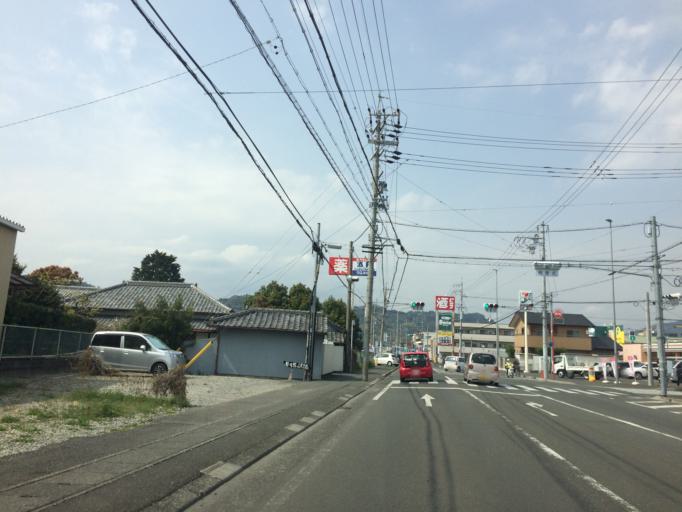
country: JP
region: Shizuoka
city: Shizuoka-shi
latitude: 34.9971
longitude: 138.3954
